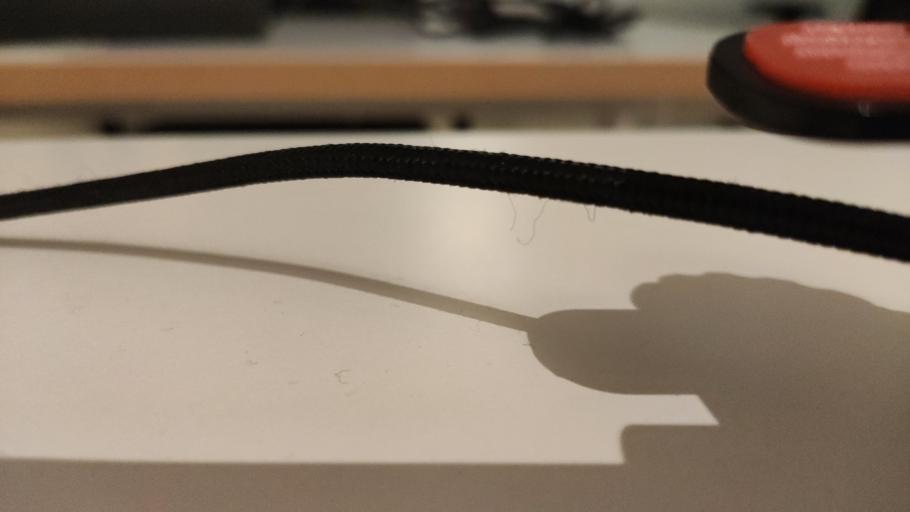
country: RU
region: Moskovskaya
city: Novoye
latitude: 55.6630
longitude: 38.9417
